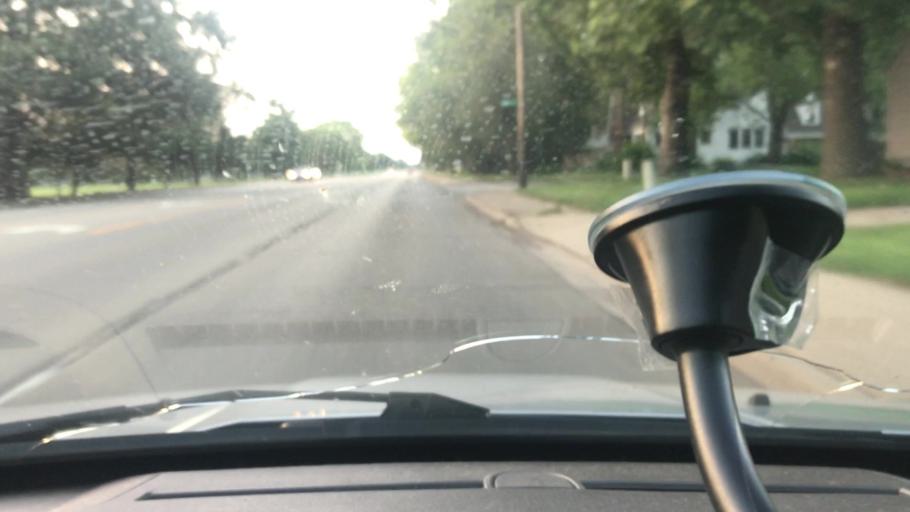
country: US
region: Illinois
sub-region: Tazewell County
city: Pekin
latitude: 40.5838
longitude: -89.6410
